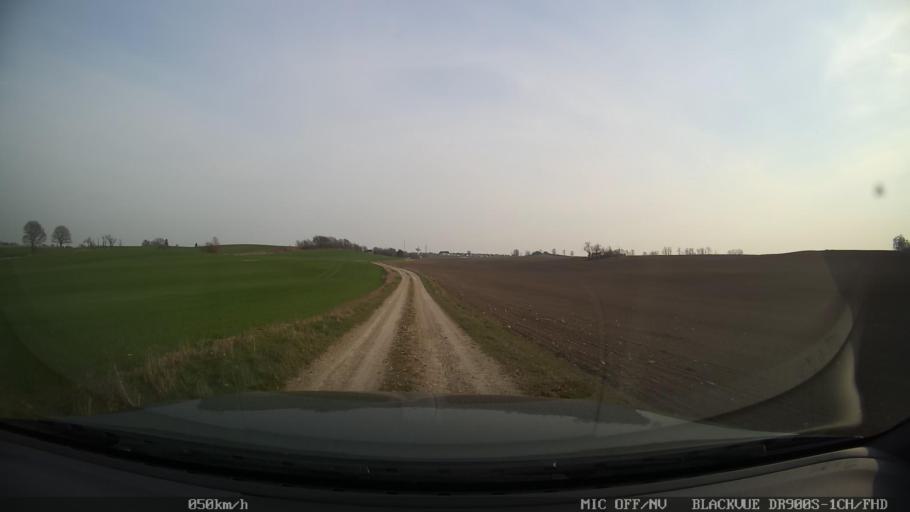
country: SE
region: Skane
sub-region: Ystads Kommun
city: Ystad
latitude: 55.4571
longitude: 13.7910
